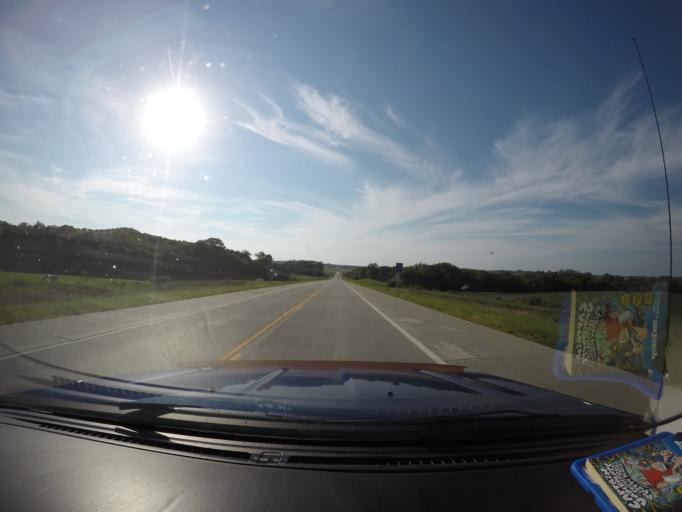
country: US
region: Kansas
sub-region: Leavenworth County
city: Leavenworth
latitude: 39.3472
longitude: -94.9654
